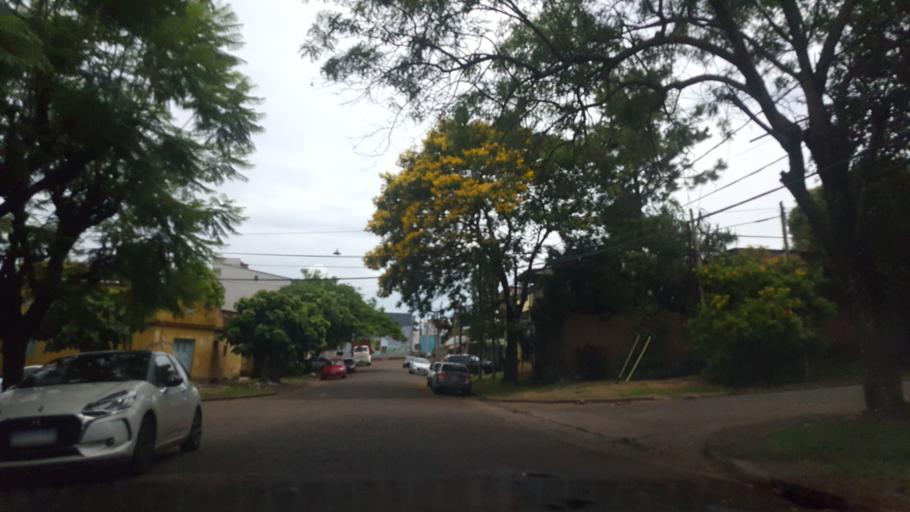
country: AR
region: Misiones
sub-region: Departamento de Capital
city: Posadas
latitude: -27.3897
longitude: -55.9020
